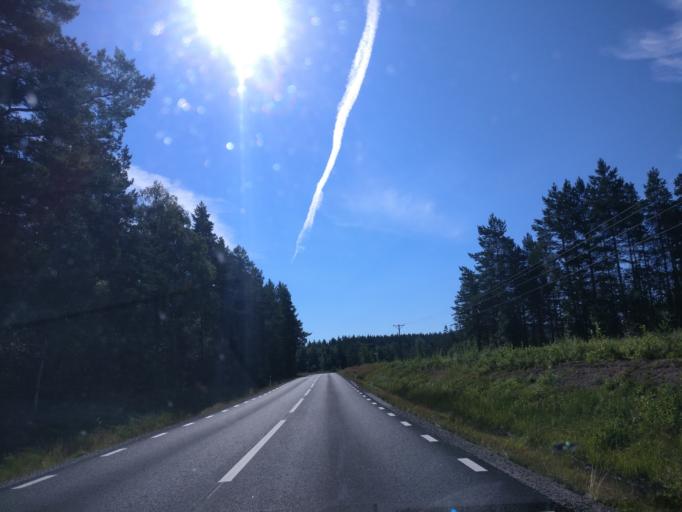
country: SE
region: Vaermland
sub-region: Hagfors Kommun
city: Hagfors
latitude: 60.0355
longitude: 13.8313
